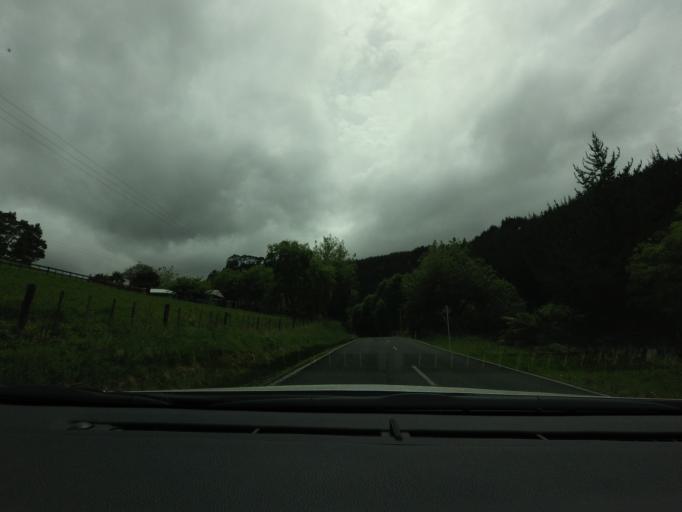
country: NZ
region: Auckland
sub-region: Auckland
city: Warkworth
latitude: -36.4970
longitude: 174.6271
